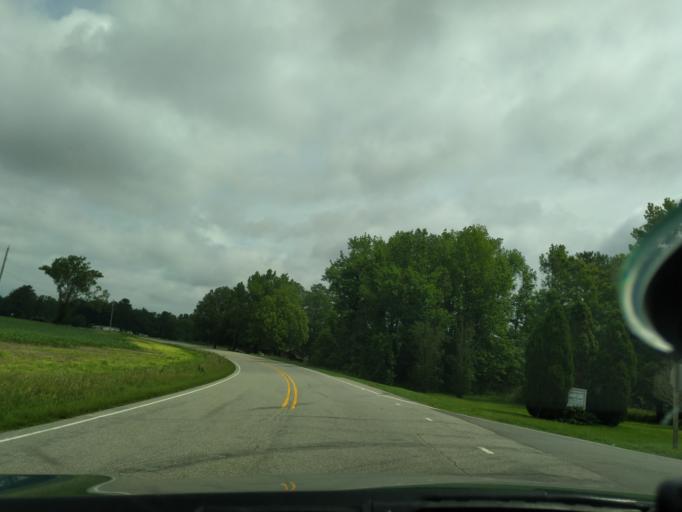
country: US
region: North Carolina
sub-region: Washington County
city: Plymouth
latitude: 35.8889
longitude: -76.6065
